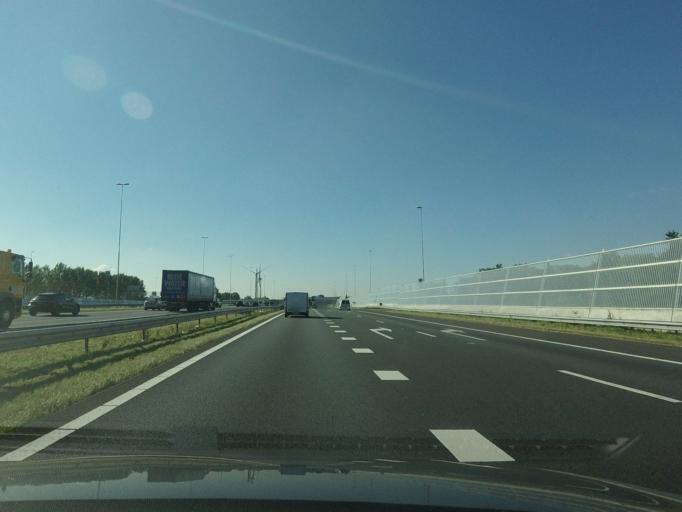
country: NL
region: South Holland
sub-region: Gemeente Leiden
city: Leiden
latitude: 52.1334
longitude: 4.4977
